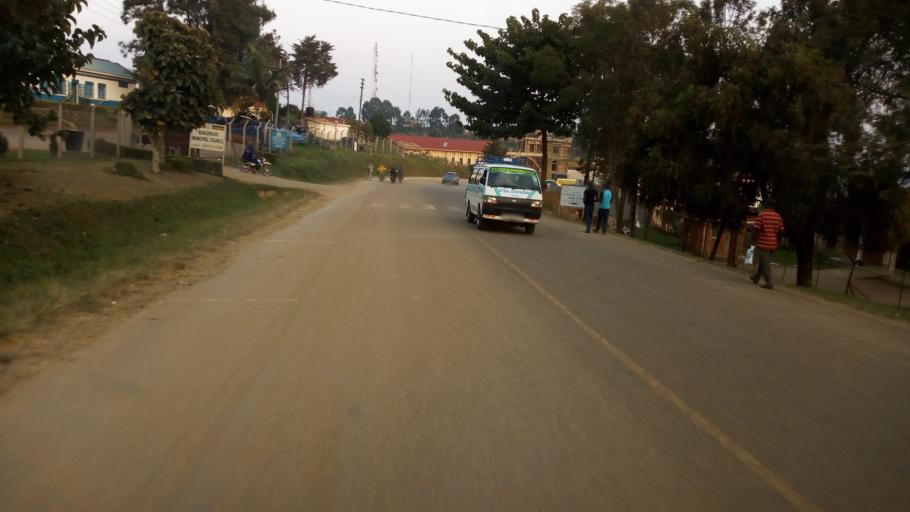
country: UG
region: Western Region
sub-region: Rukungiri District
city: Rukungiri
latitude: -0.7845
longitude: 29.9262
